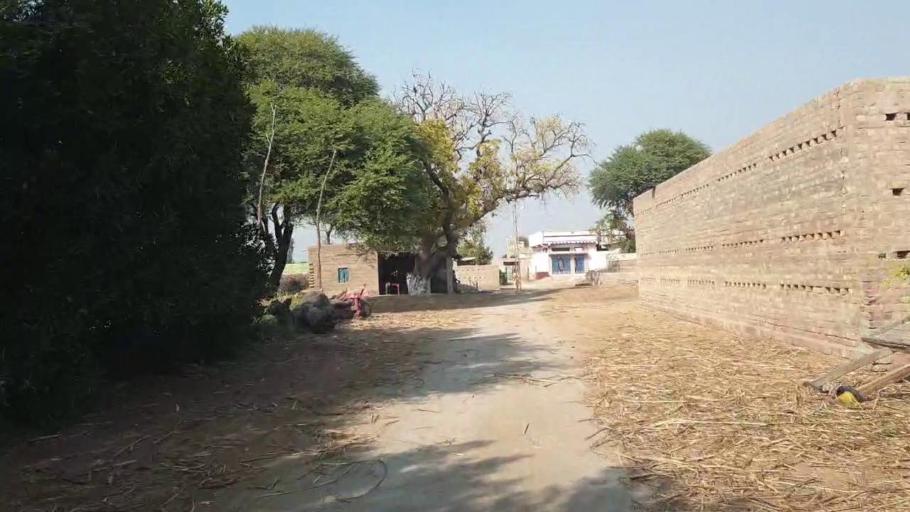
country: PK
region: Sindh
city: Mirwah Gorchani
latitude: 25.3049
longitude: 68.9514
